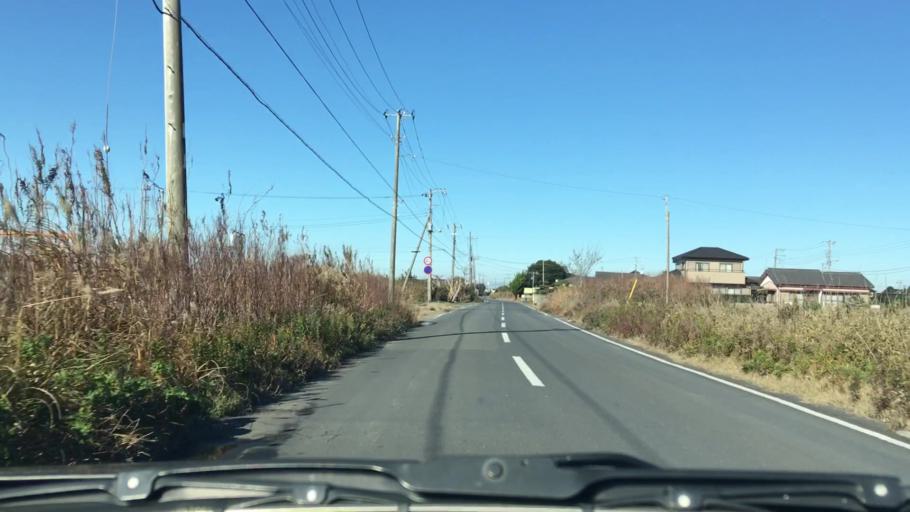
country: JP
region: Chiba
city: Omigawa
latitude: 35.8743
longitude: 140.6343
